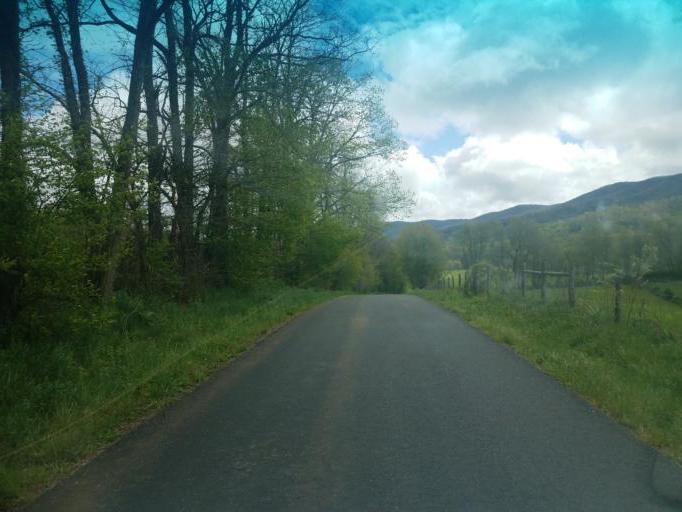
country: US
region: Virginia
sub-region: Smyth County
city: Atkins
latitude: 36.9405
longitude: -81.4234
